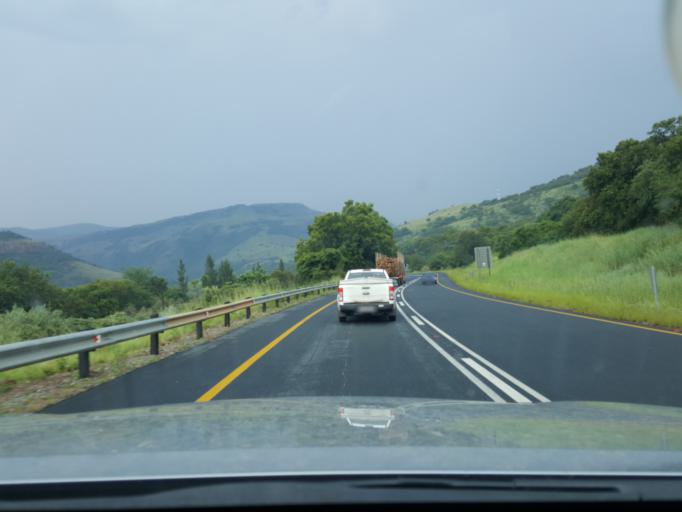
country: ZA
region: Mpumalanga
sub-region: Nkangala District Municipality
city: Belfast
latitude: -25.6336
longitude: 30.3943
